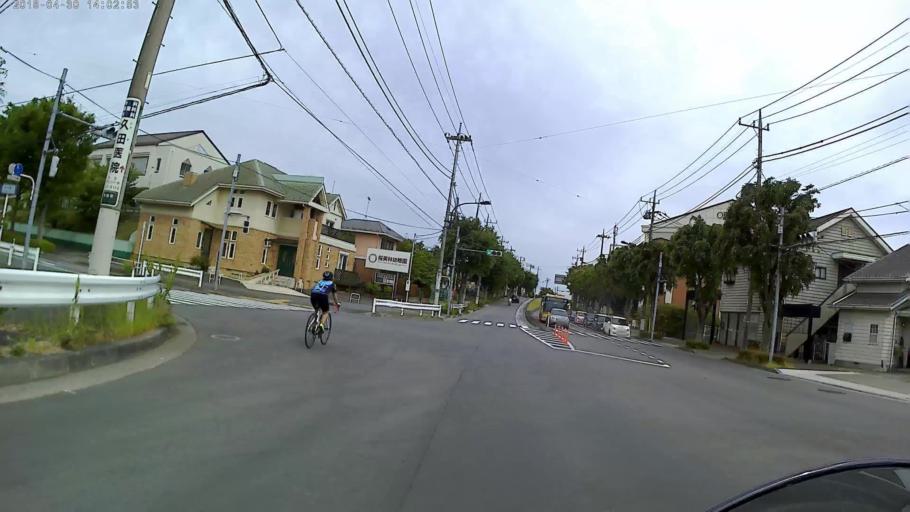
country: JP
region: Tokyo
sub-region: Machida-shi
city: Machida
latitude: 35.5833
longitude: 139.4051
